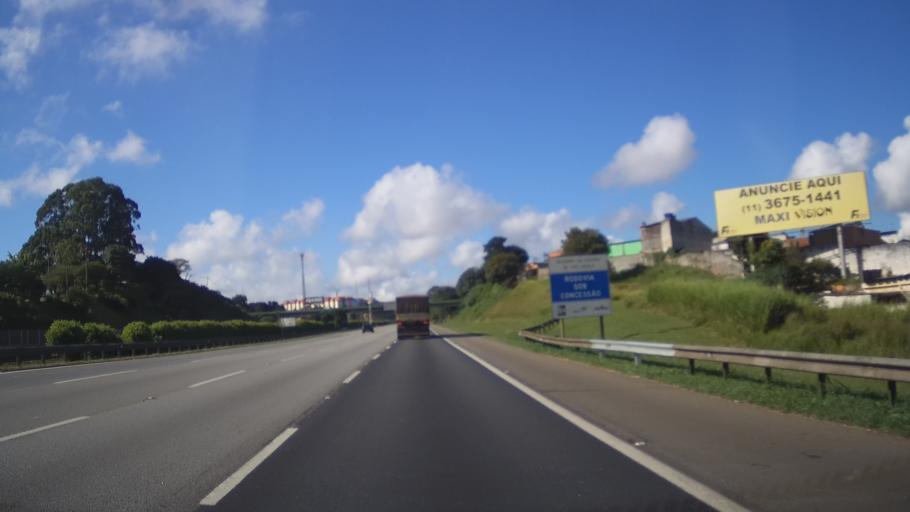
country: BR
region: Sao Paulo
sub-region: Diadema
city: Diadema
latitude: -23.6916
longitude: -46.6043
